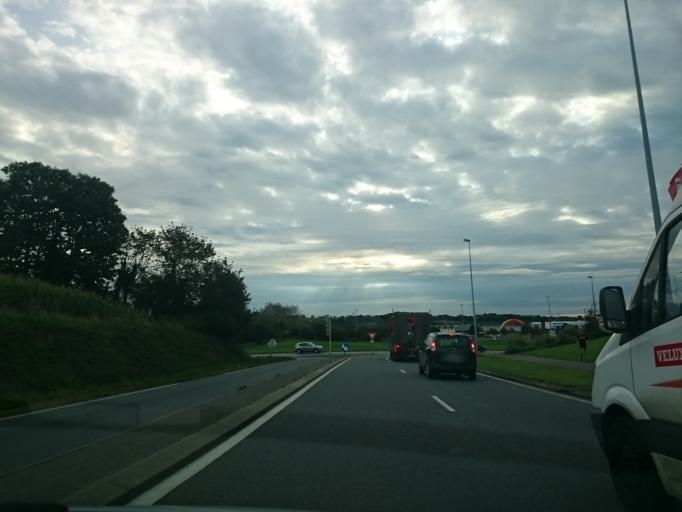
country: FR
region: Brittany
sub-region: Departement du Finistere
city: Gouesnou
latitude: 48.4189
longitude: -4.4410
